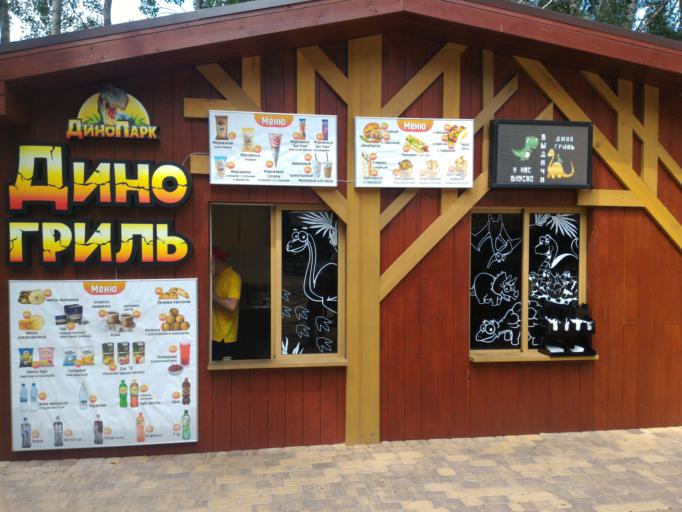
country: RU
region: Belgorod
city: Razumnoye
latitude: 50.5531
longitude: 36.6438
